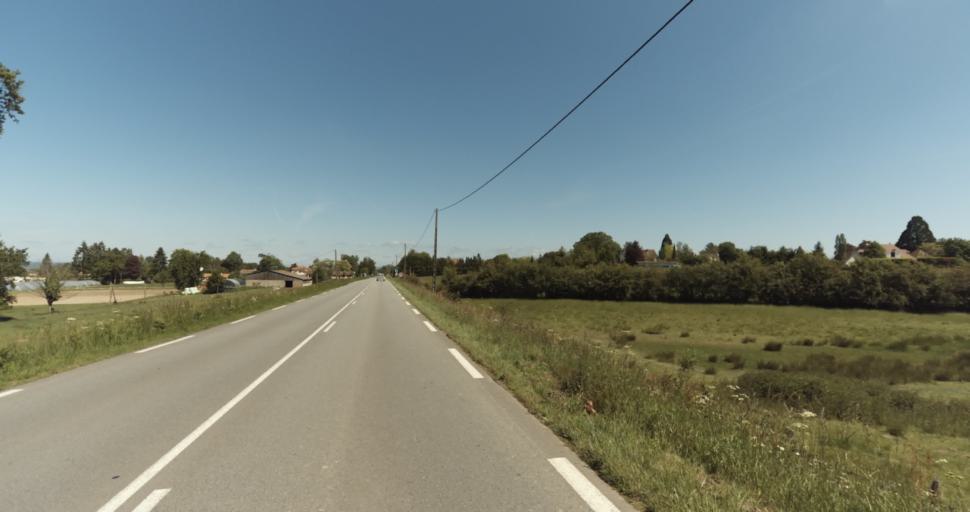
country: FR
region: Limousin
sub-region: Departement de la Haute-Vienne
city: Condat-sur-Vienne
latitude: 45.7795
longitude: 1.2889
